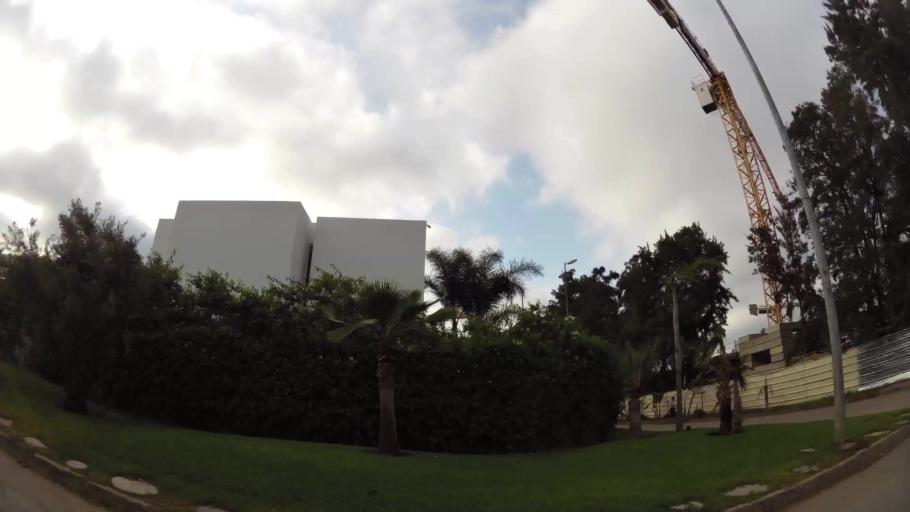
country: MA
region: Rabat-Sale-Zemmour-Zaer
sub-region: Rabat
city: Rabat
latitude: 33.9502
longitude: -6.8429
